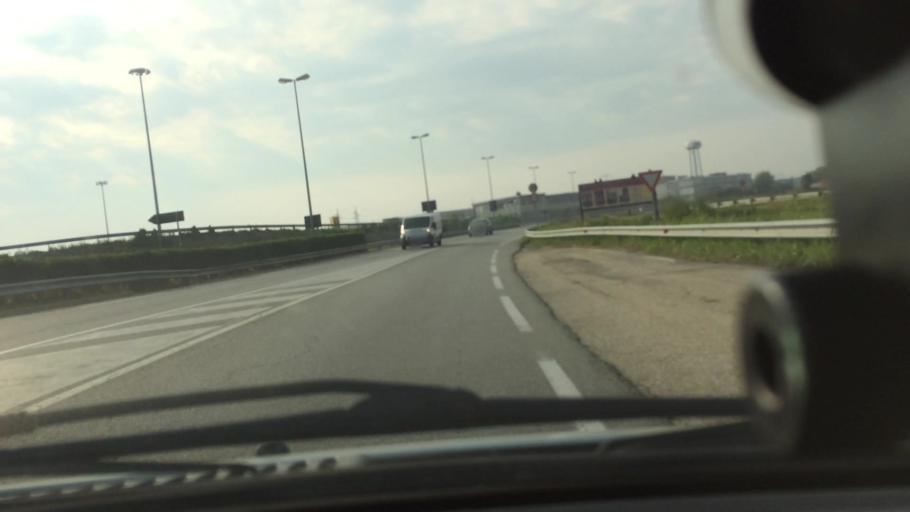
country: IT
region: Piedmont
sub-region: Provincia di Torino
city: Villastellone
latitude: 44.9164
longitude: 7.7422
